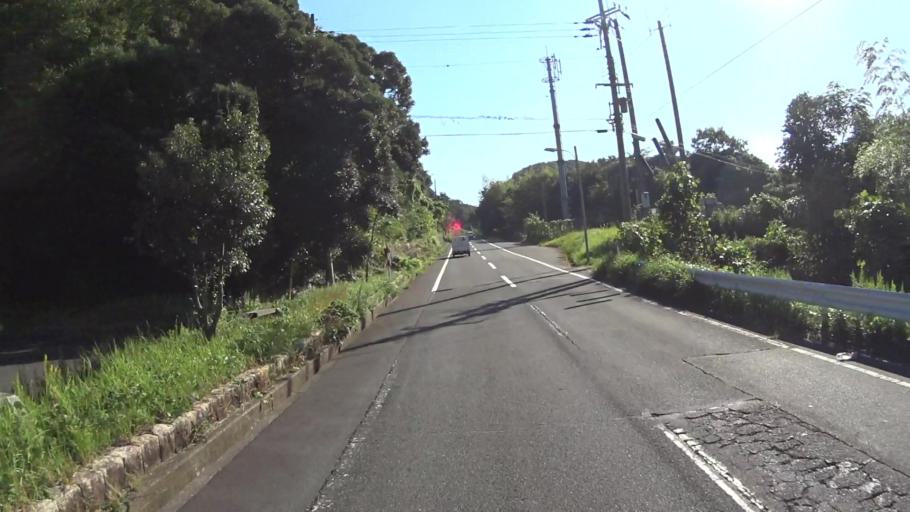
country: JP
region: Kyoto
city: Miyazu
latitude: 35.7066
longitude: 135.0693
